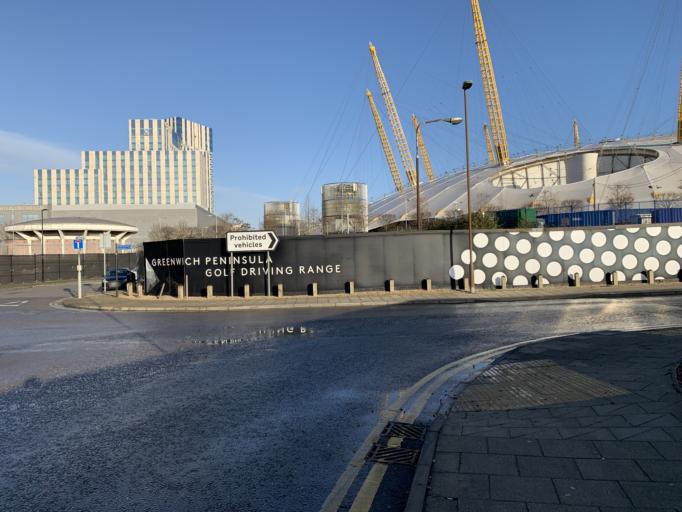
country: GB
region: England
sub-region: Greater London
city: Poplar
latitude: 51.5007
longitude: 0.0008
